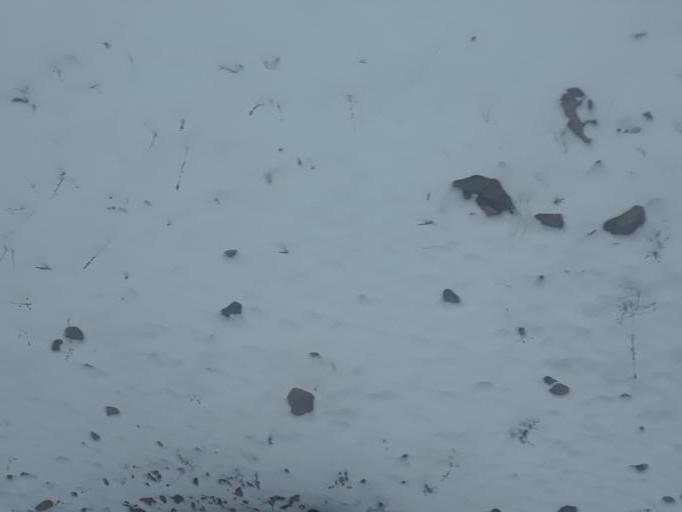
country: US
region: Colorado
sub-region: Boulder County
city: Coal Creek
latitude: 39.9253
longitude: -105.4216
